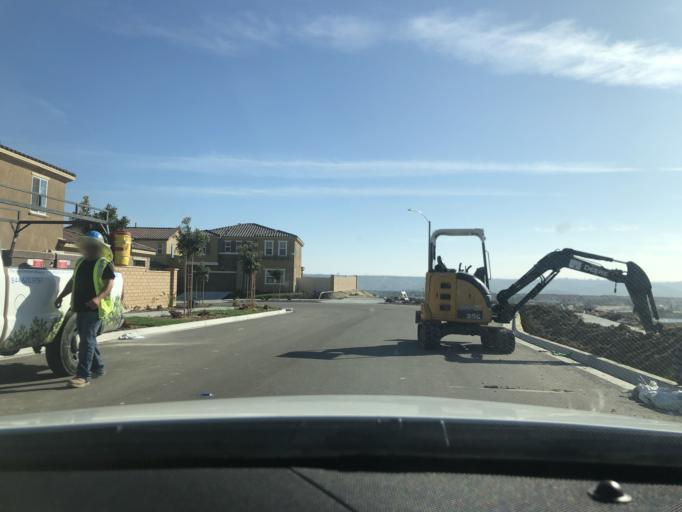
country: US
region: California
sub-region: San Diego County
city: Bonita
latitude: 32.6069
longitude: -116.9966
